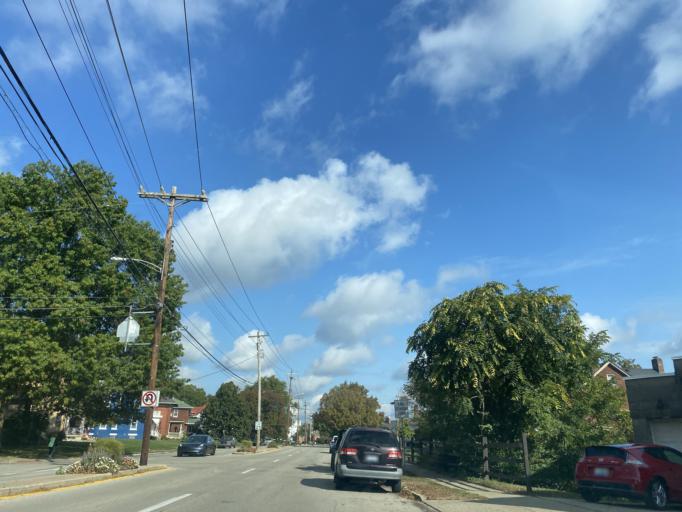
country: US
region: Kentucky
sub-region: Campbell County
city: Fort Thomas
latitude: 39.0738
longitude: -84.4471
